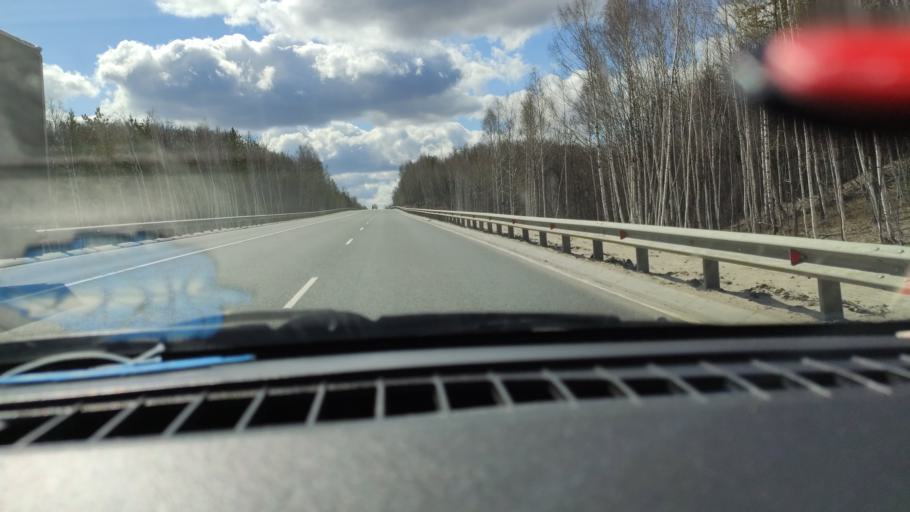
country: RU
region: Saratov
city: Khvalynsk
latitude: 52.4960
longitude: 48.0149
